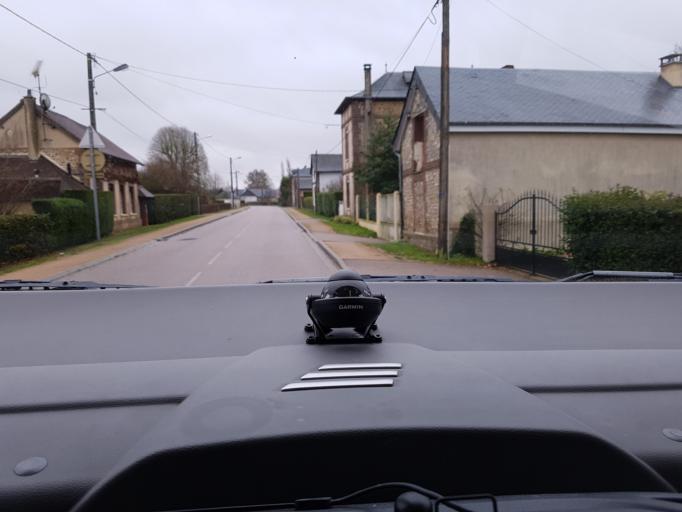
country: FR
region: Haute-Normandie
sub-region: Departement de l'Eure
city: Pont-Saint-Pierre
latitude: 49.3150
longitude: 1.3055
